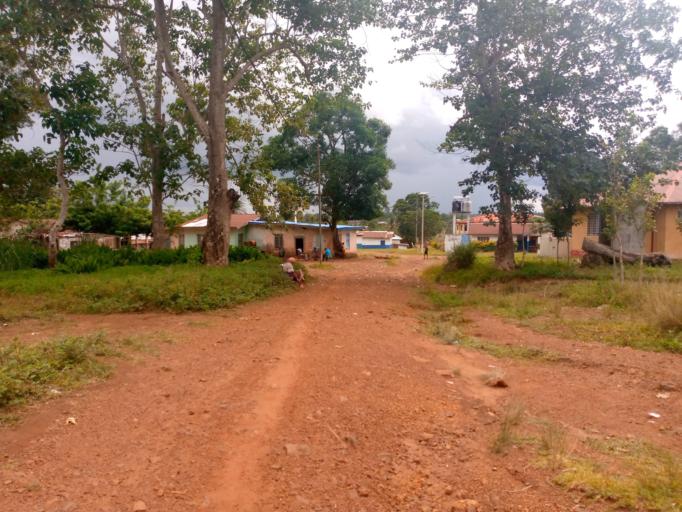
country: SL
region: Southern Province
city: Mogbwemo
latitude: 7.6039
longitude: -12.1737
